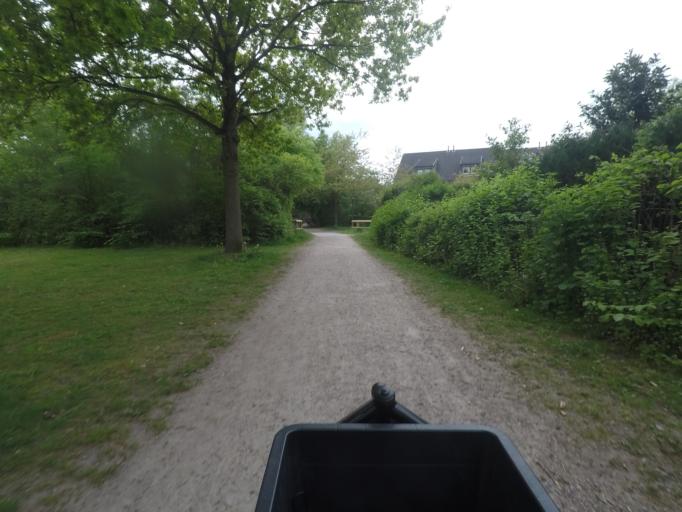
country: DE
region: Hamburg
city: Sasel
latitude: 53.6319
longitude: 10.1120
